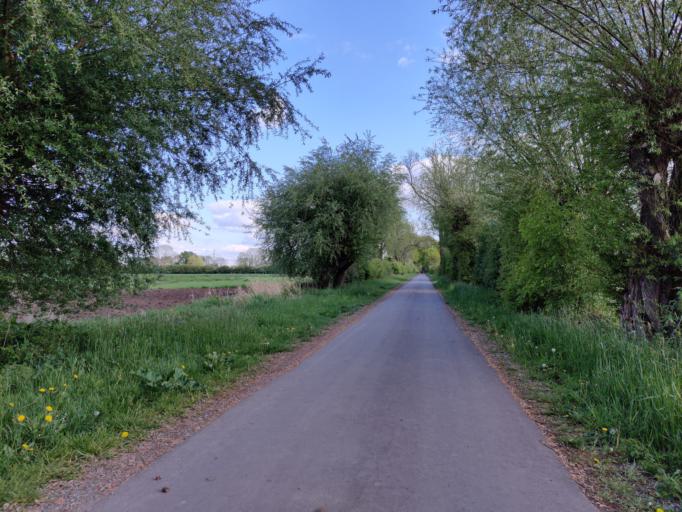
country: DE
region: Lower Saxony
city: Wunstorf
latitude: 52.4399
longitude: 9.4754
